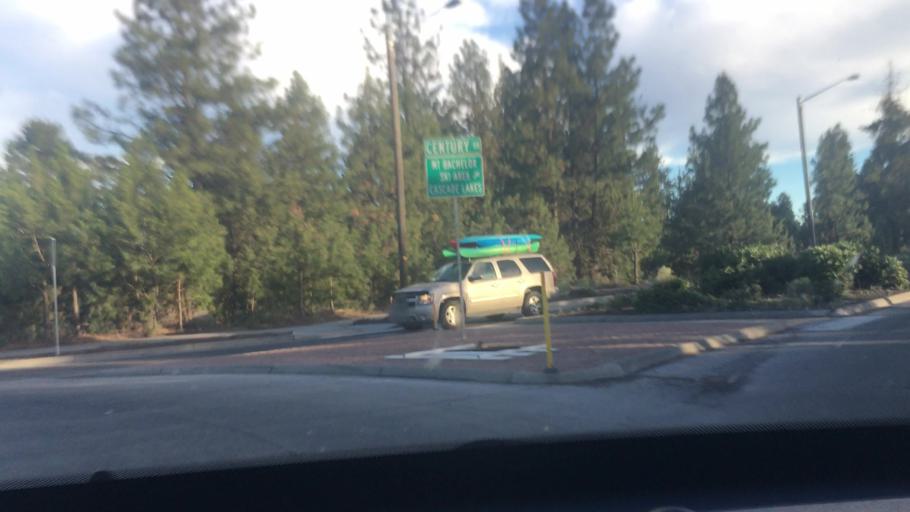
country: US
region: Oregon
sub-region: Deschutes County
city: Bend
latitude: 44.0385
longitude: -121.3363
